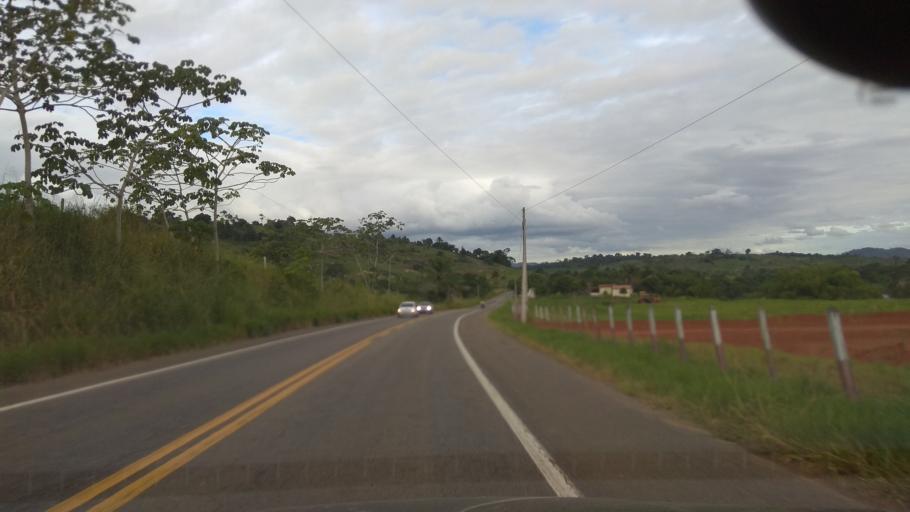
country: BR
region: Bahia
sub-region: Ipiau
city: Ipiau
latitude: -14.1795
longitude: -39.6655
